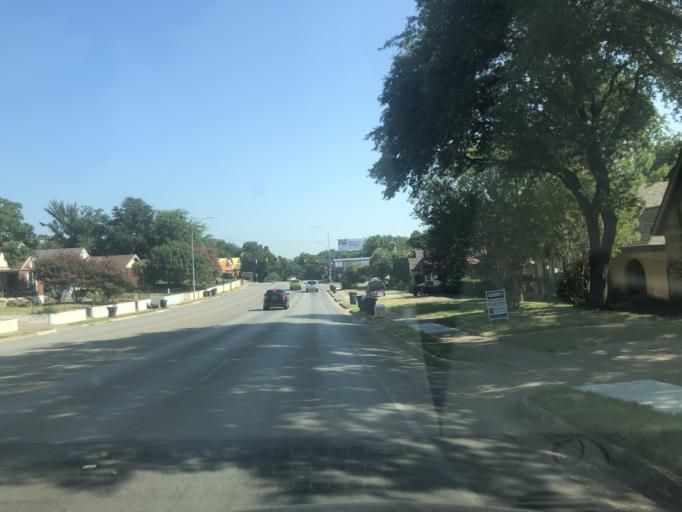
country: US
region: Texas
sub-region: Tarrant County
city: Fort Worth
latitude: 32.7149
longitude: -97.3603
